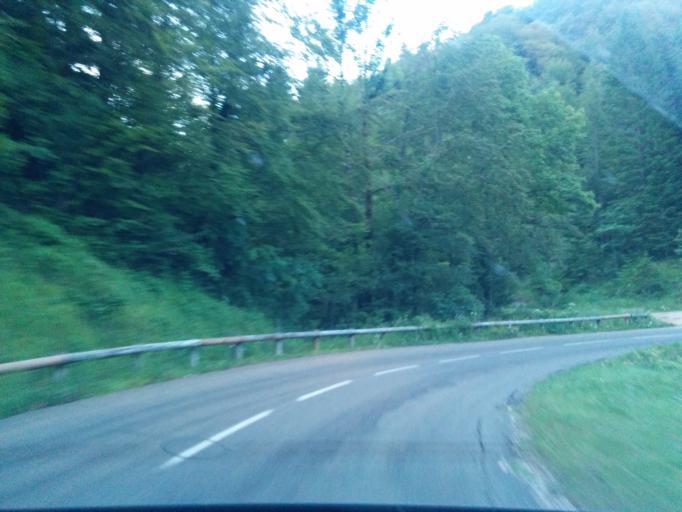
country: FR
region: Franche-Comte
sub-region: Departement du Jura
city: Valfin-les-Saint-Claude
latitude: 46.4499
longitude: 5.8062
